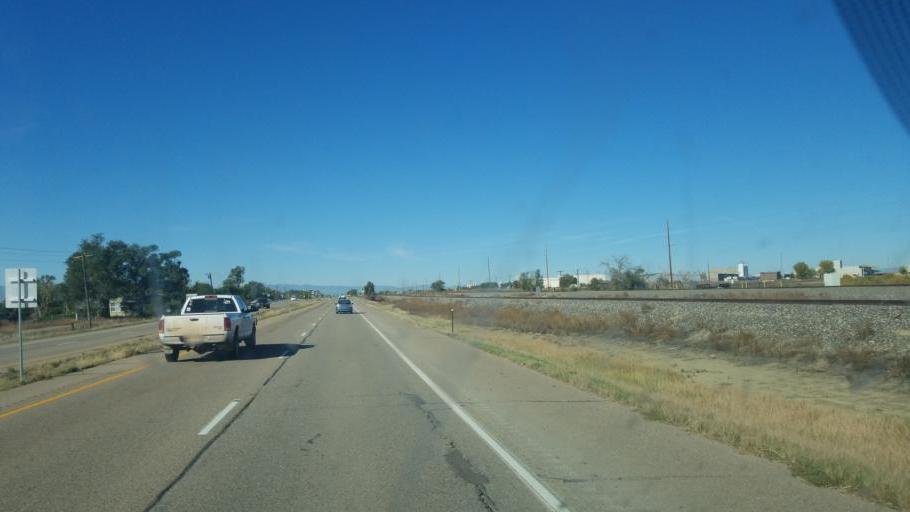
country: US
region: Colorado
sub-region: Pueblo County
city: Pueblo
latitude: 38.2758
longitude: -104.4756
